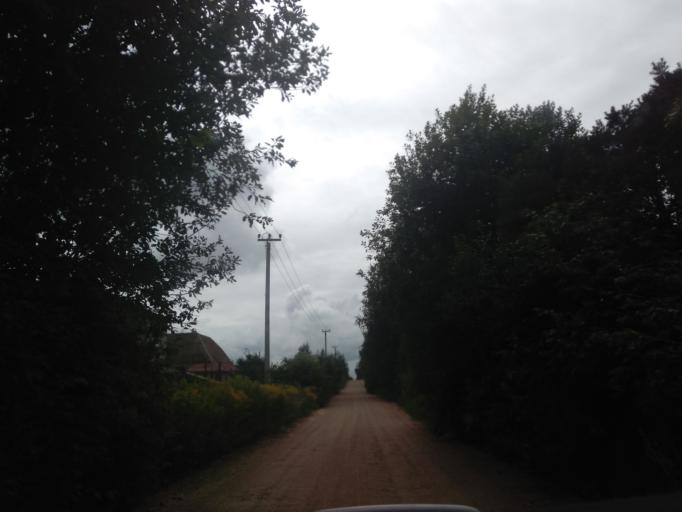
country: BY
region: Minsk
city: Slabada
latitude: 53.9903
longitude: 27.9111
